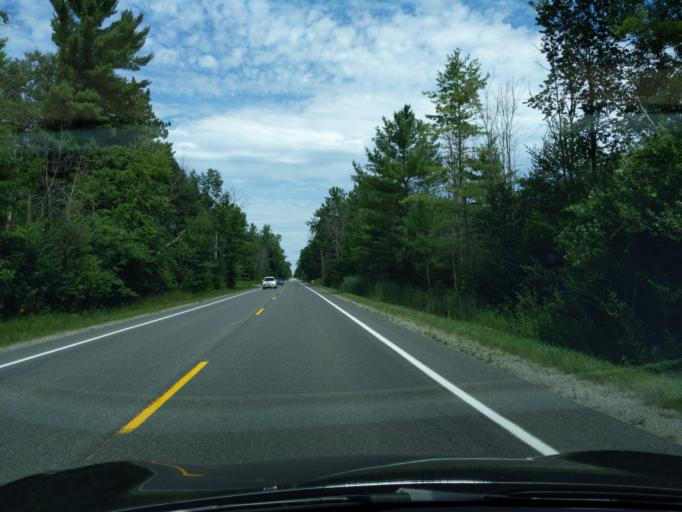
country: US
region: Michigan
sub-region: Midland County
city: Midland
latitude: 43.5881
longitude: -84.3693
